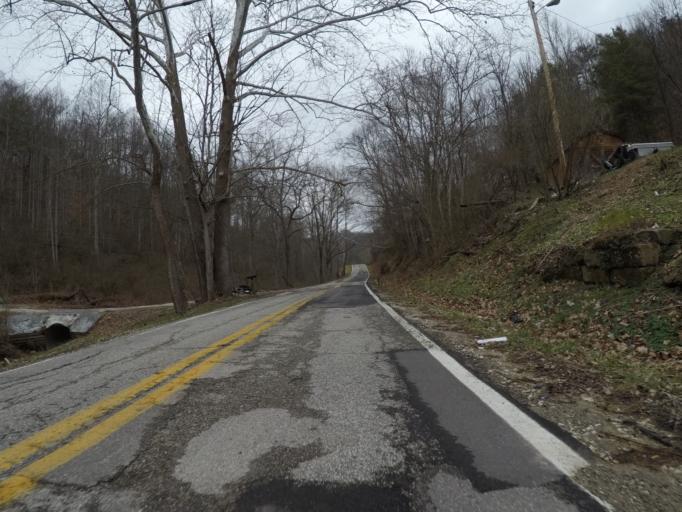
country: US
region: West Virginia
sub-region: Cabell County
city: Lesage
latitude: 38.4632
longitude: -82.2773
